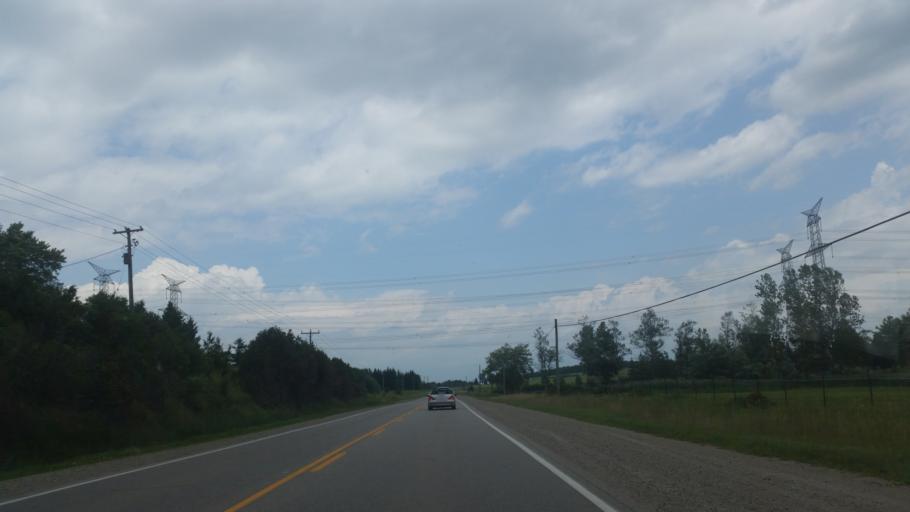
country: CA
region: Ontario
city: Orangeville
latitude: 43.7209
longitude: -80.1090
